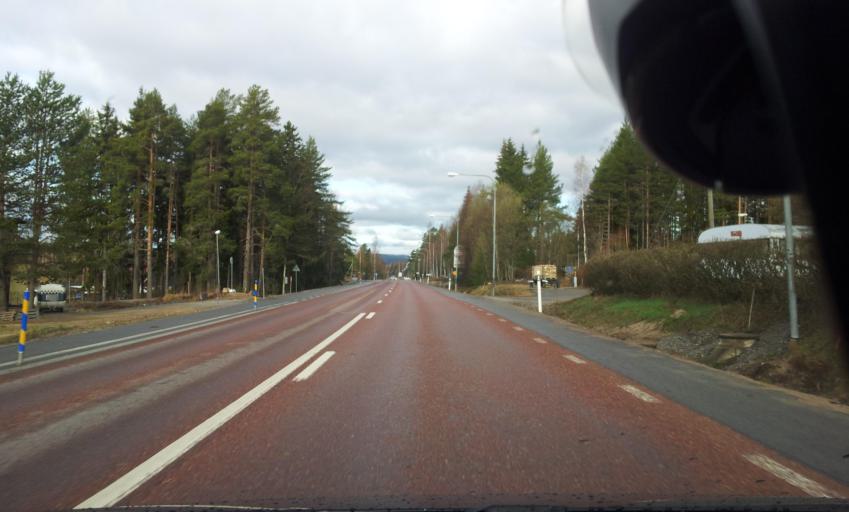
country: SE
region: Gaevleborg
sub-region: Ljusdals Kommun
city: Ljusdal
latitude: 61.8249
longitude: 16.1414
